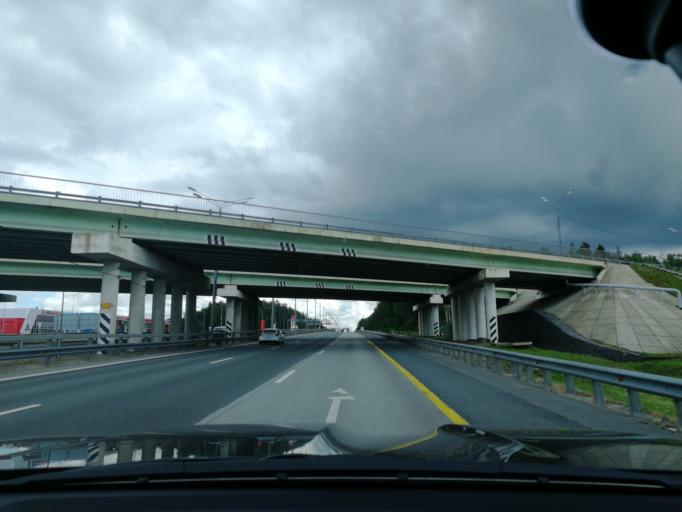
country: RU
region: Moskovskaya
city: Barybino
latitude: 55.2366
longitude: 37.8693
